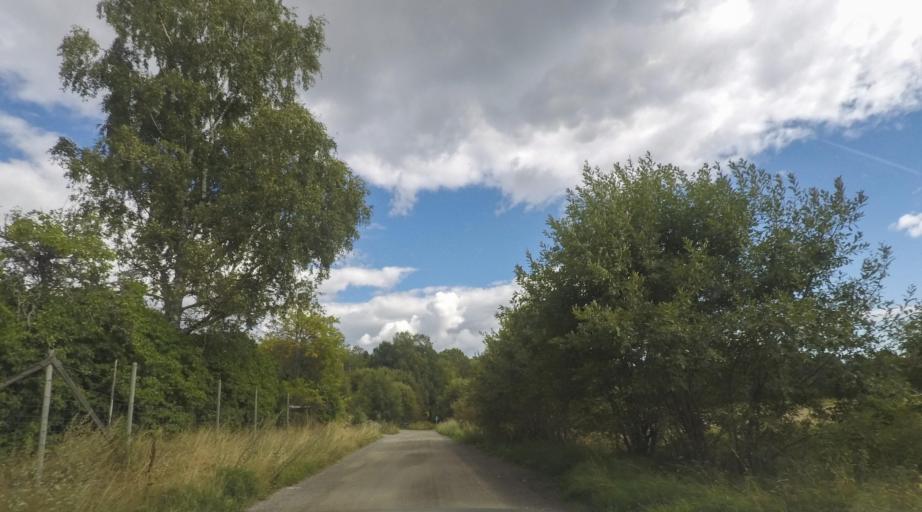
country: SE
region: Stockholm
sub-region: Sodertalje Kommun
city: Pershagen
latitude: 59.1204
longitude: 17.6538
